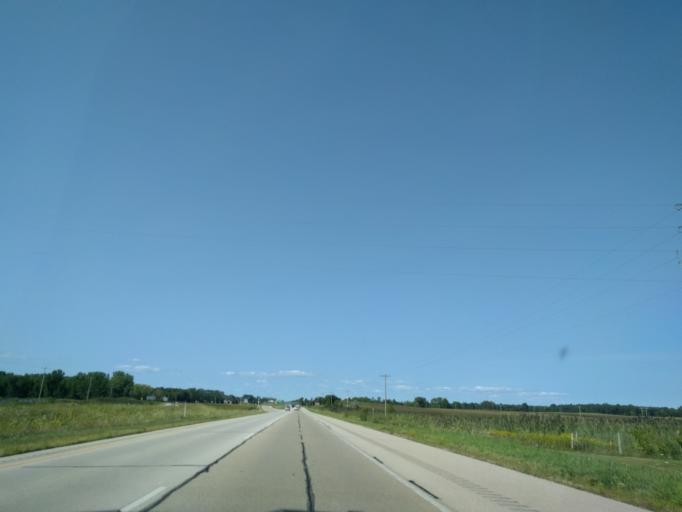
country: US
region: Wisconsin
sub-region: Brown County
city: Suamico
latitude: 44.7354
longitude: -88.0506
